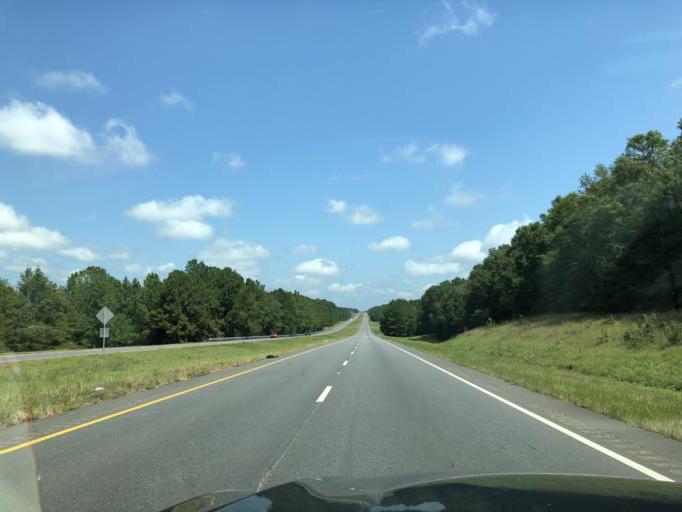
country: US
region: Alabama
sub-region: Henry County
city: Headland
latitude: 31.4611
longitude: -85.3075
